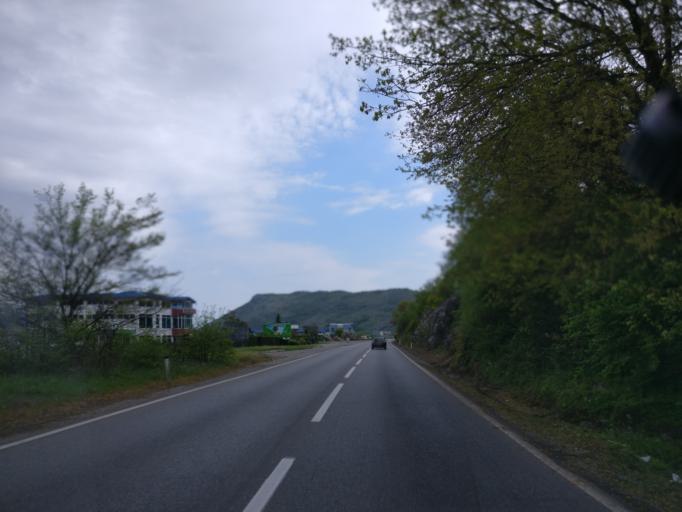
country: ME
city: Spuz
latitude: 42.4746
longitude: 19.1719
